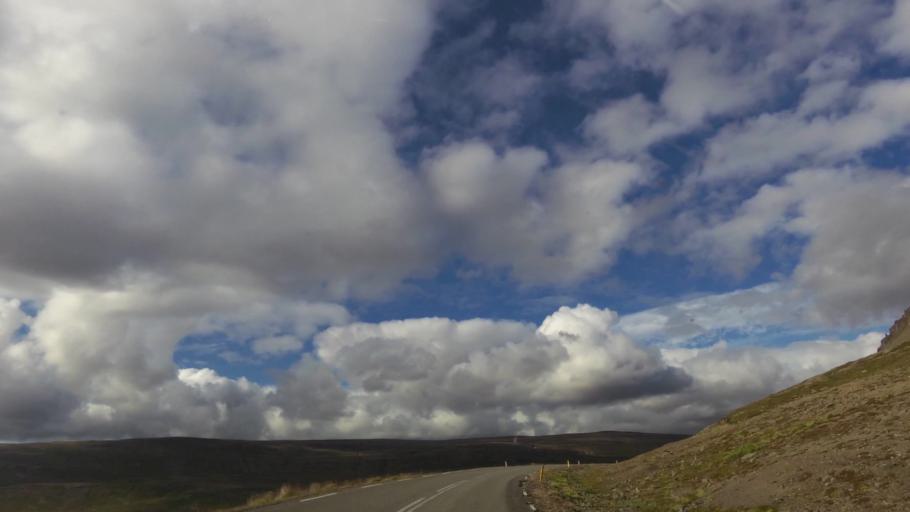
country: IS
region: West
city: Olafsvik
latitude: 65.5208
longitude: -23.8335
